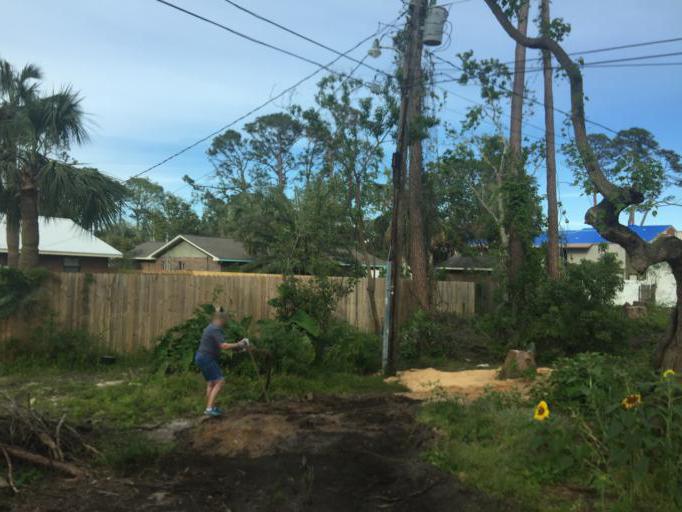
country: US
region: Florida
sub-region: Bay County
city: Lower Grand Lagoon
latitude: 30.1615
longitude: -85.7673
